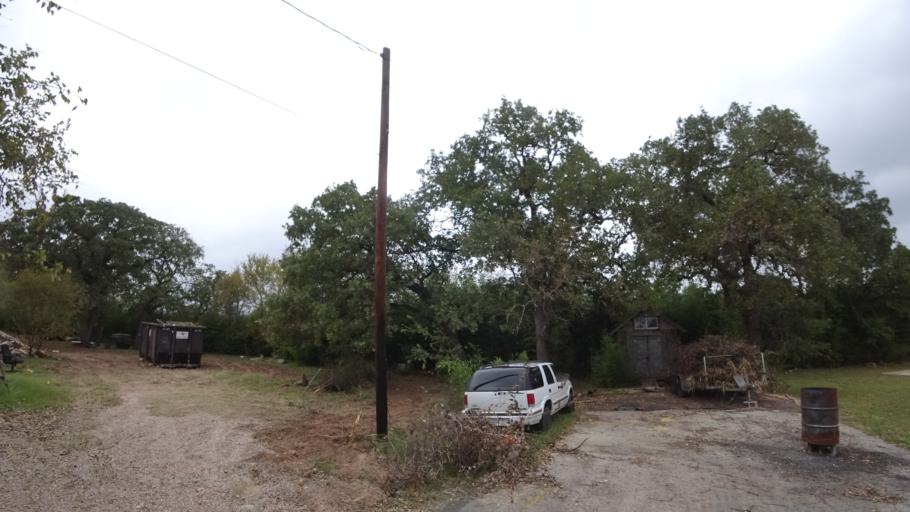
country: US
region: Texas
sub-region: Travis County
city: Bee Cave
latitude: 30.3337
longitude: -97.9250
